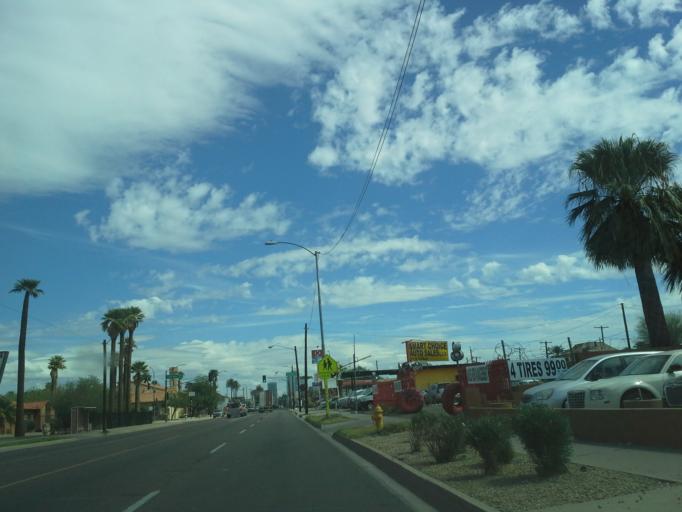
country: US
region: Arizona
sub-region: Maricopa County
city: Phoenix
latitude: 33.4512
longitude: -112.1059
